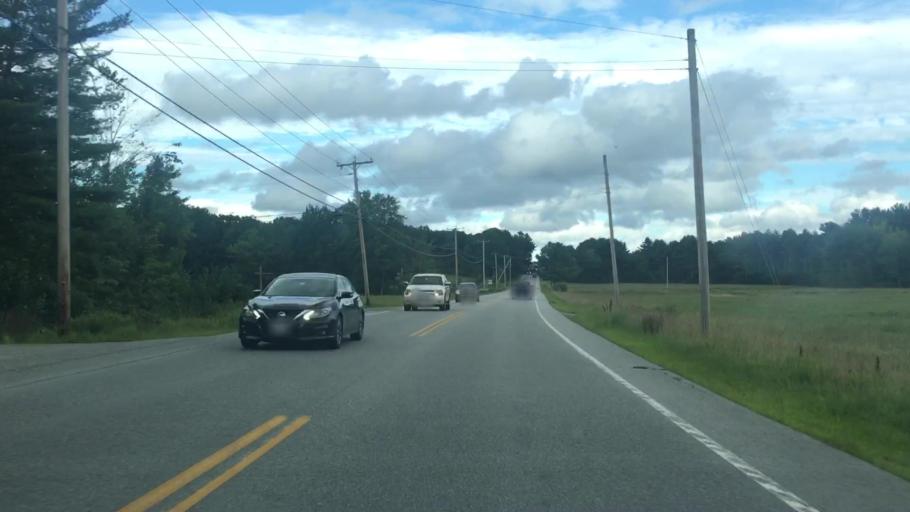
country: US
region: Maine
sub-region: York County
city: Dayton
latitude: 43.5447
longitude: -70.5375
